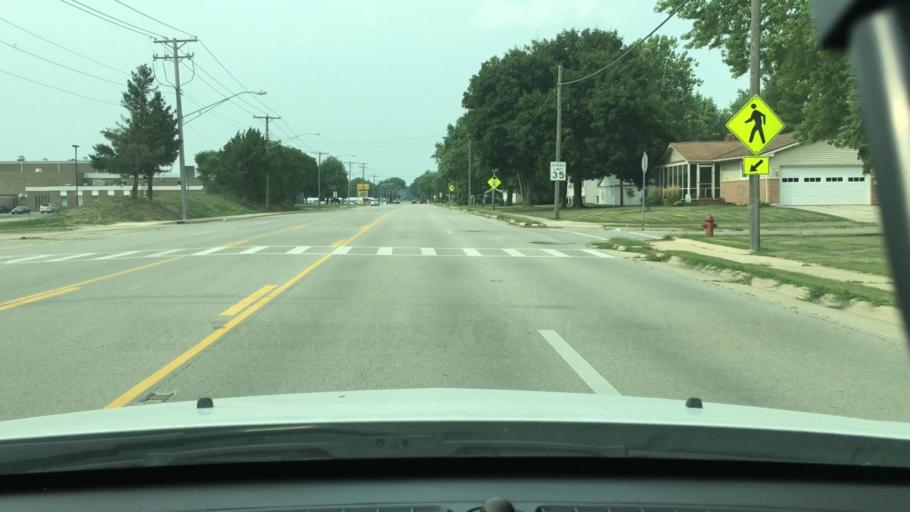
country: US
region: Illinois
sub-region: DeKalb County
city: DeKalb
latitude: 41.9094
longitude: -88.7535
